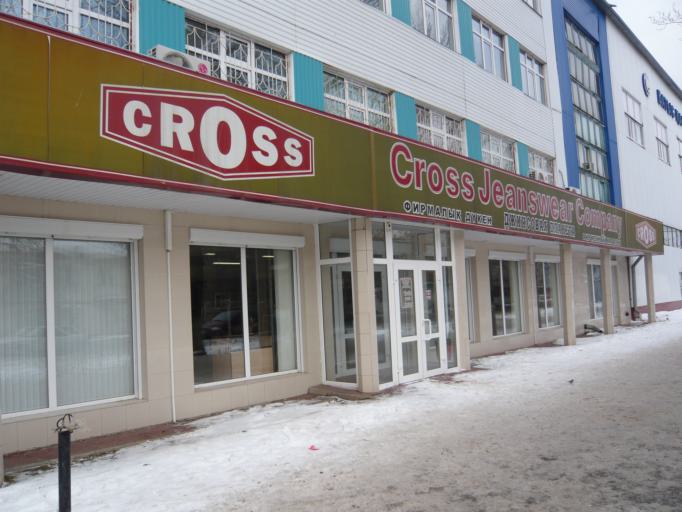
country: KZ
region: Batys Qazaqstan
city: Oral
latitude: 51.2147
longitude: 51.3640
